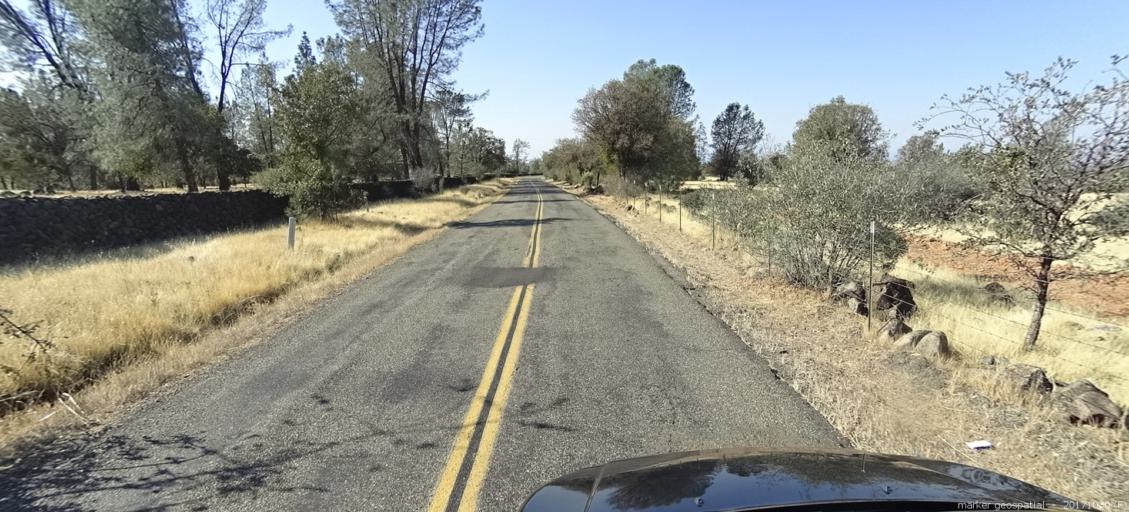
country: US
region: California
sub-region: Shasta County
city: Shingletown
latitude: 40.6391
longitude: -121.9535
